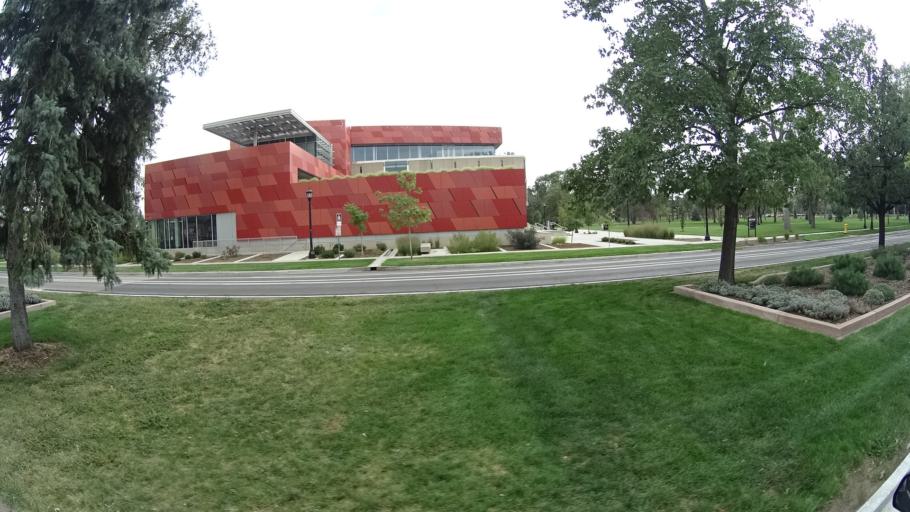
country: US
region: Colorado
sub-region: El Paso County
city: Colorado Springs
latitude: 38.8489
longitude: -104.8246
